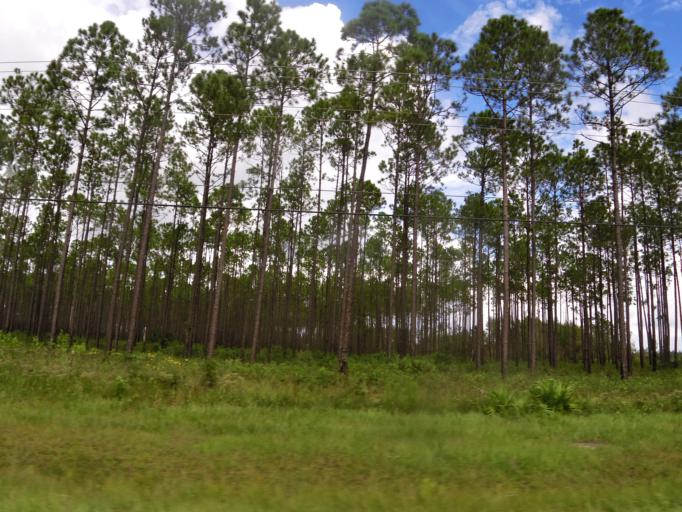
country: US
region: Florida
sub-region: Duval County
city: Baldwin
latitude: 30.1487
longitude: -82.0200
